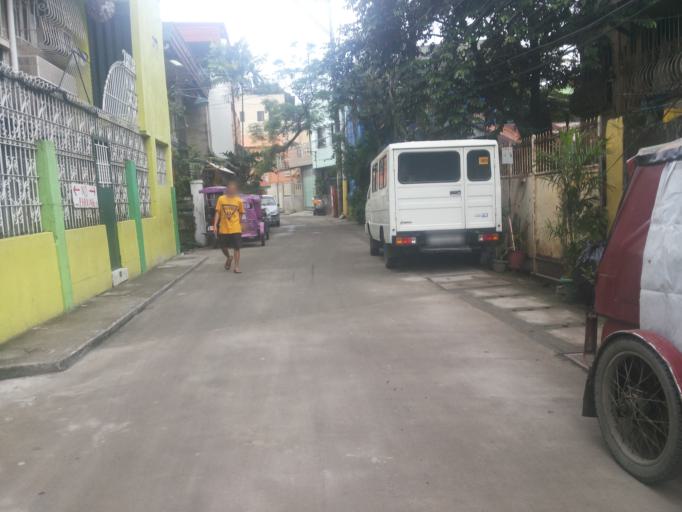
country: PH
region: Calabarzon
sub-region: Province of Rizal
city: Pateros
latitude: 14.5551
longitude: 121.0890
